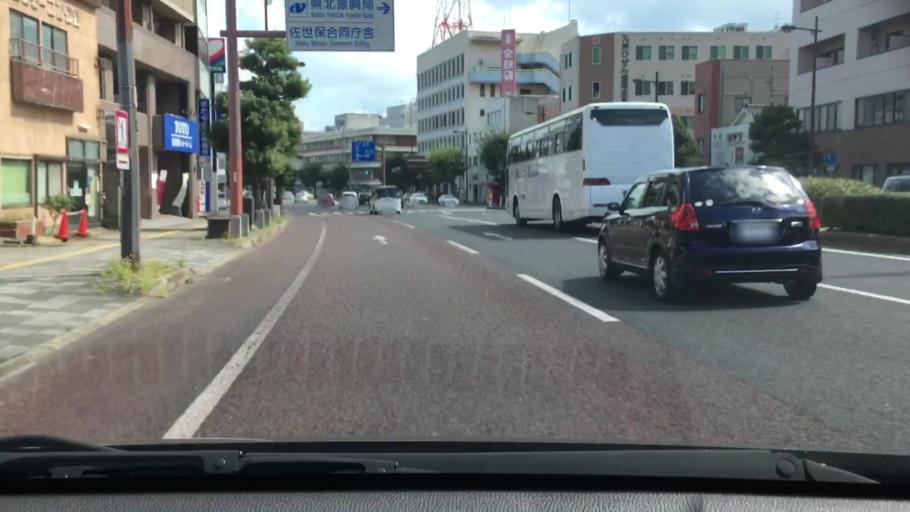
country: JP
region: Nagasaki
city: Sasebo
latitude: 33.1792
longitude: 129.7161
